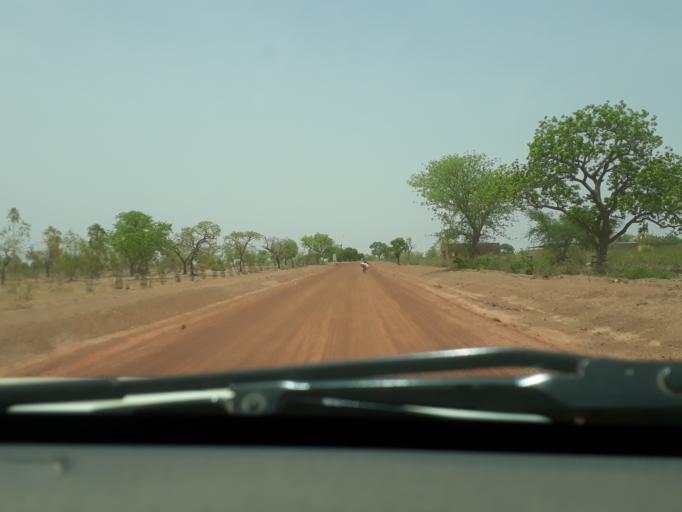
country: BF
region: Plateau-Central
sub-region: Province d'Oubritenga
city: Ziniare
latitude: 12.5793
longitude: -1.3329
